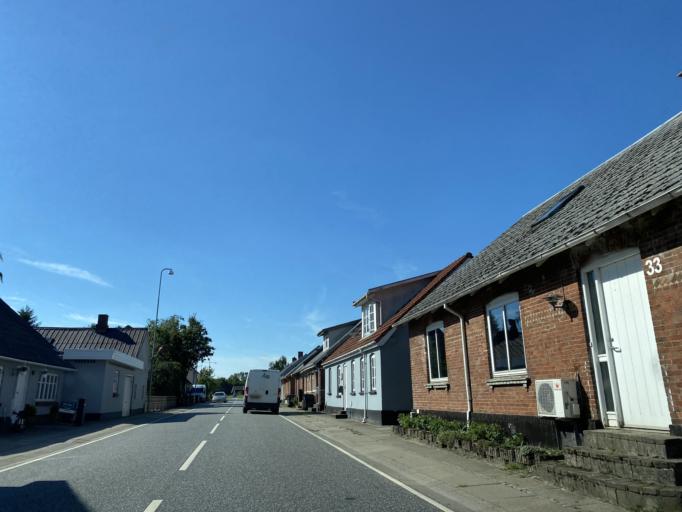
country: DK
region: Central Jutland
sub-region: Hedensted Kommune
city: Torring
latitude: 55.8614
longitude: 9.4158
